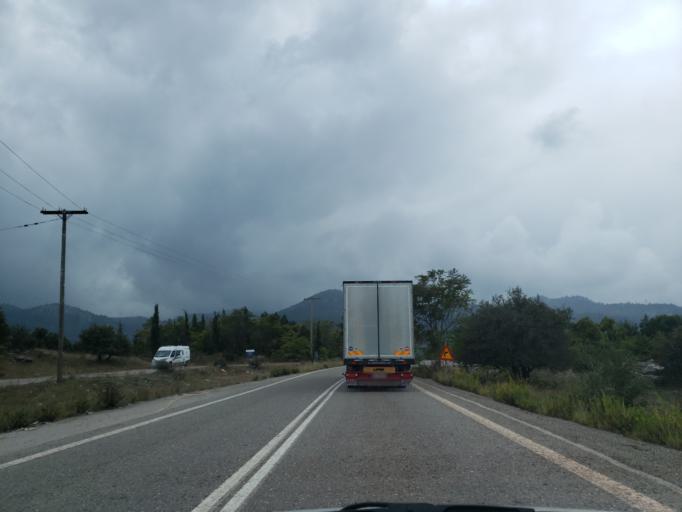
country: GR
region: Central Greece
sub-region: Nomos Fokidos
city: Amfissa
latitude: 38.6407
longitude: 22.3962
